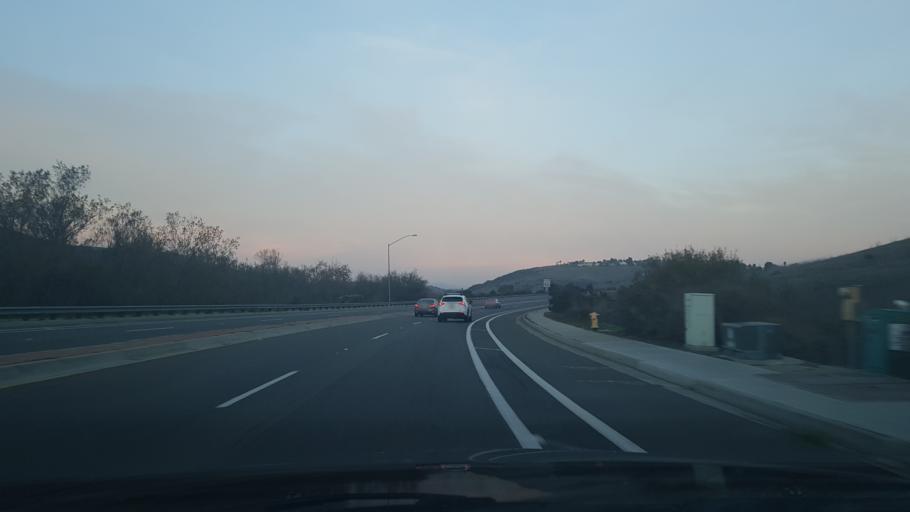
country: US
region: California
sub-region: San Diego County
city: Del Mar
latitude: 32.9063
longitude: -117.2135
